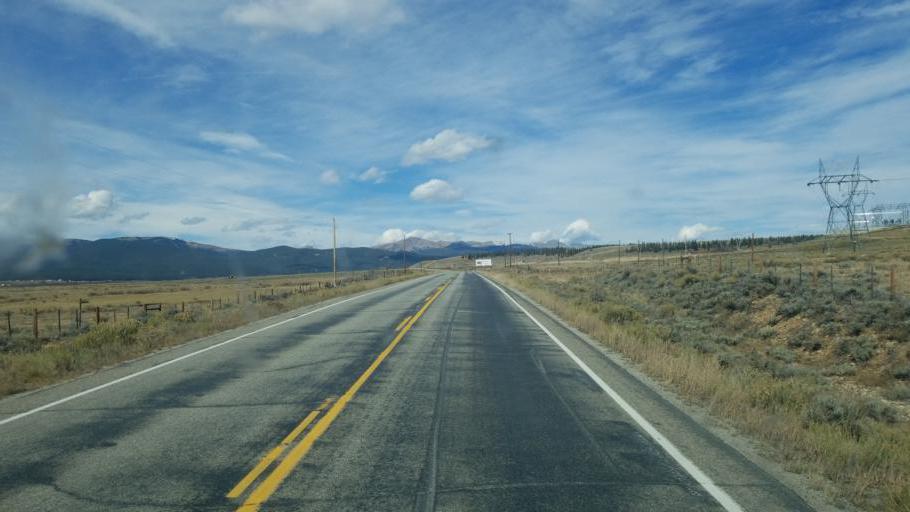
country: US
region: Colorado
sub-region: Lake County
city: Leadville
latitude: 39.1826
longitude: -106.3274
